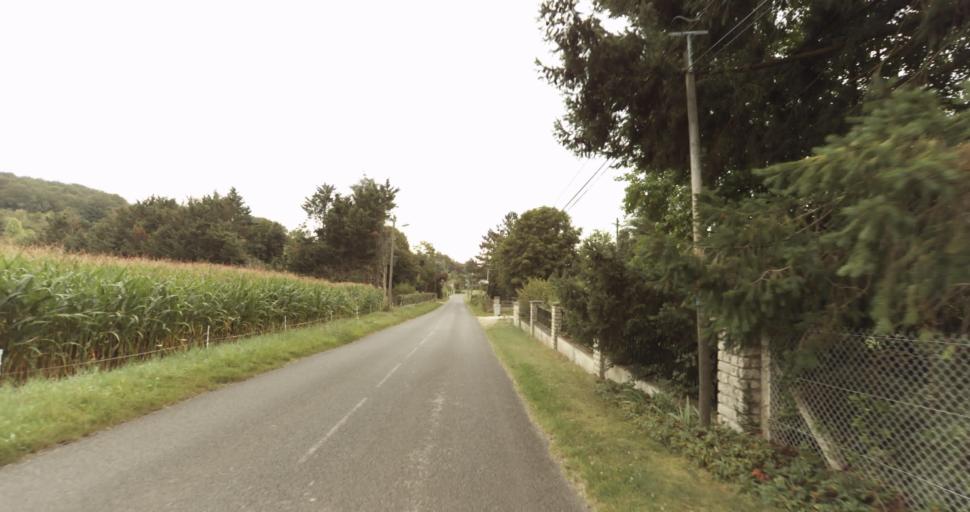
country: FR
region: Haute-Normandie
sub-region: Departement de l'Eure
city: Marcilly-sur-Eure
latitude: 48.8265
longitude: 1.3283
